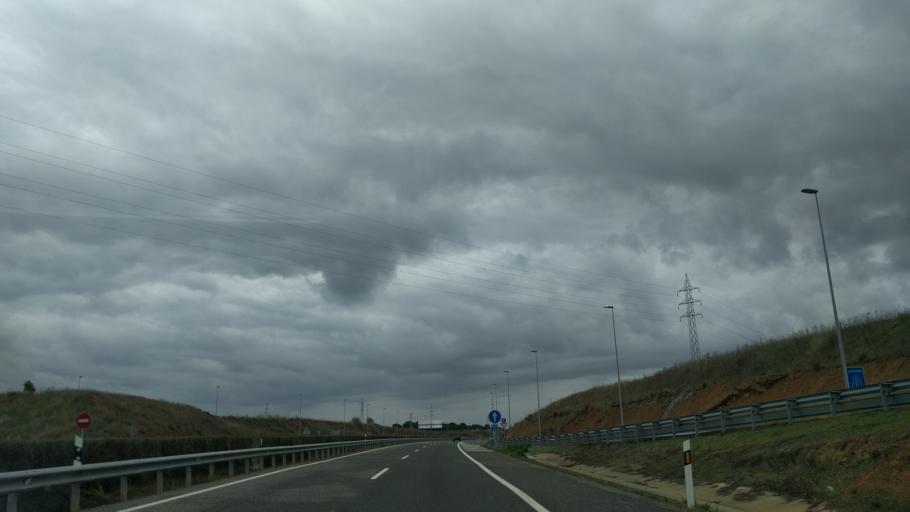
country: ES
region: Aragon
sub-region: Provincia de Huesca
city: Castejon del Puente
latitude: 41.9519
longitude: 0.1860
